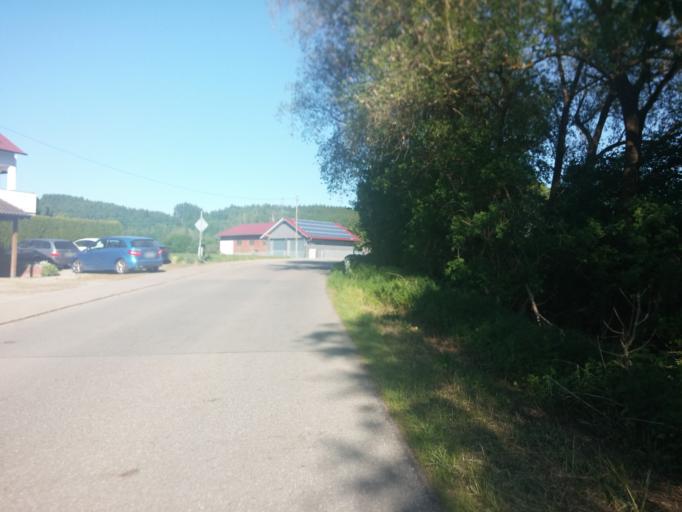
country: DE
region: Bavaria
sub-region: Swabia
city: Lautrach
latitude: 47.9007
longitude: 10.1318
